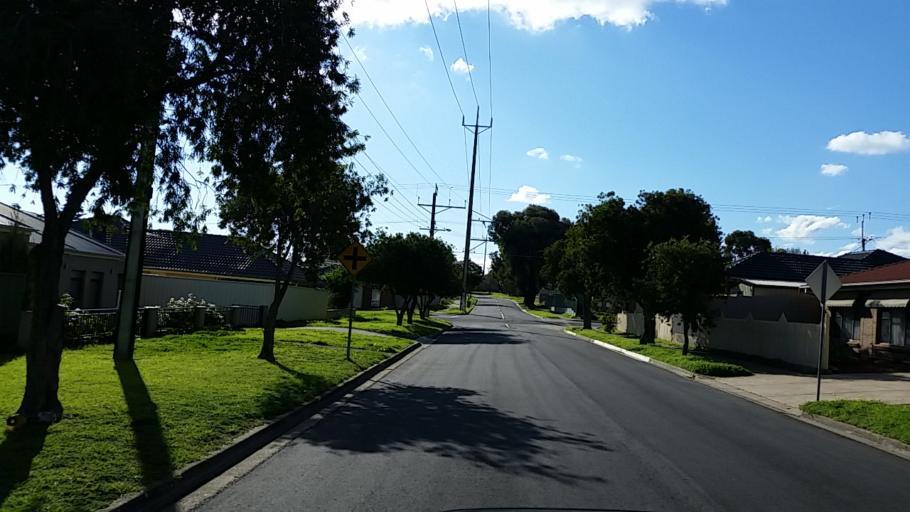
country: AU
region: South Australia
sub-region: Tea Tree Gully
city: Modbury
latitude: -34.8509
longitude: 138.6750
